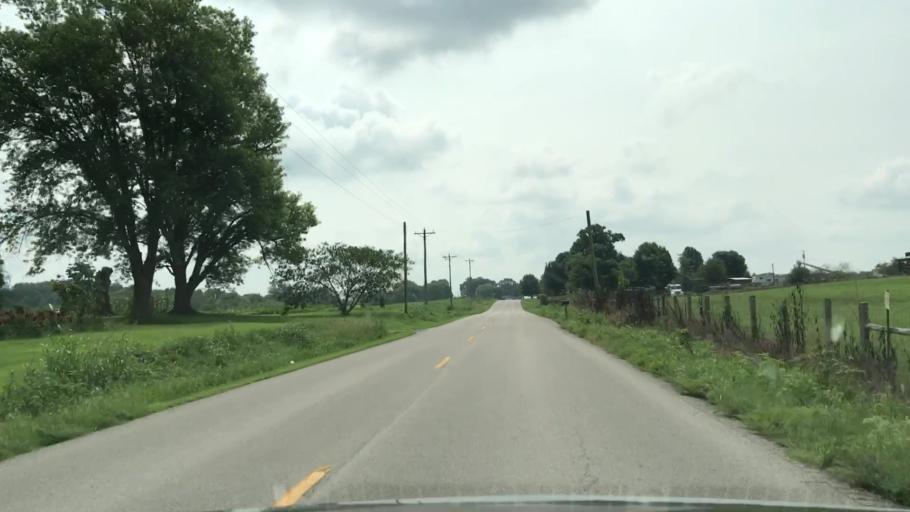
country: US
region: Kentucky
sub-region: Edmonson County
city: Brownsville
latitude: 37.1370
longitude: -86.1769
